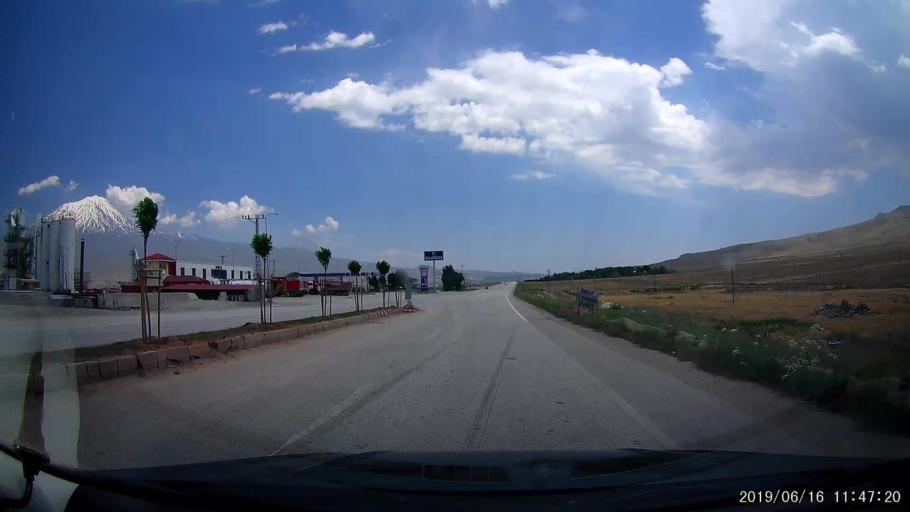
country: TR
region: Agri
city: Dogubayazit
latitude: 39.5583
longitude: 44.1288
